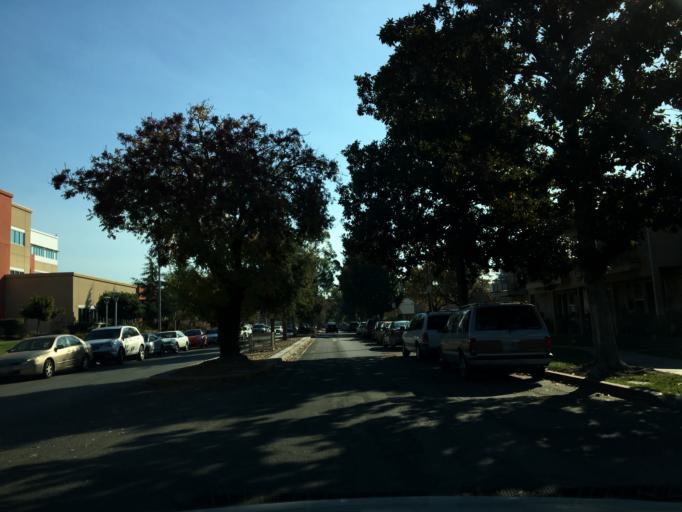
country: US
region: California
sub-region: Santa Clara County
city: Alum Rock
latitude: 37.3619
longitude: -121.8514
